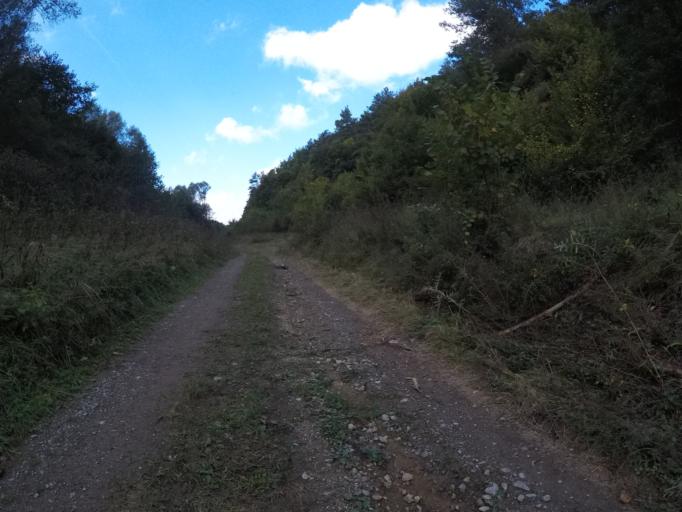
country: SK
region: Presovsky
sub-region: Okres Presov
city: Presov
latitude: 48.9302
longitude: 21.1697
